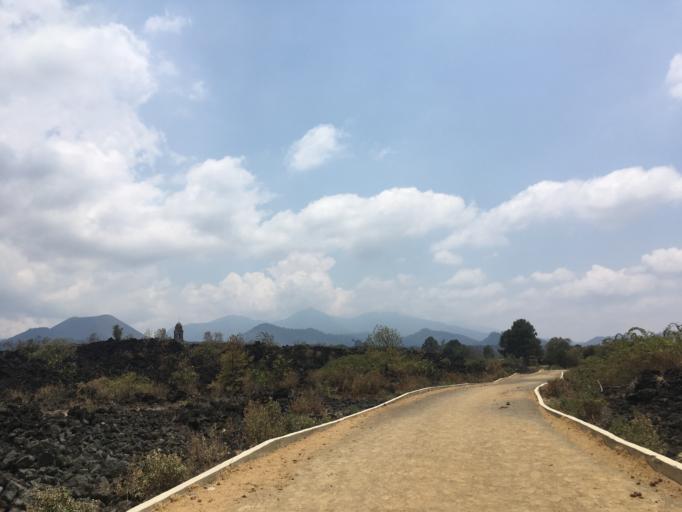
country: MX
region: Michoacan
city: Angahuan
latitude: 19.5367
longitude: -102.2465
